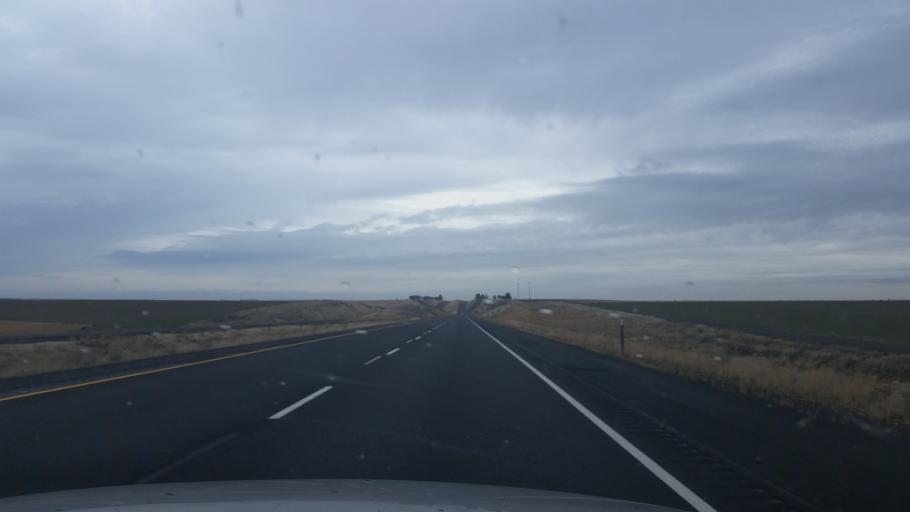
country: US
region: Washington
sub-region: Grant County
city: Warden
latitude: 47.0863
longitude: -118.8180
